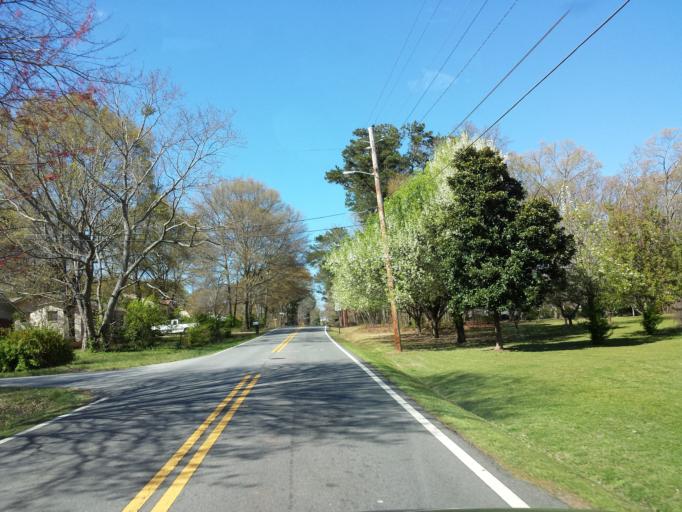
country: US
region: Georgia
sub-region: Cobb County
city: Fair Oaks
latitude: 33.9088
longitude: -84.5533
